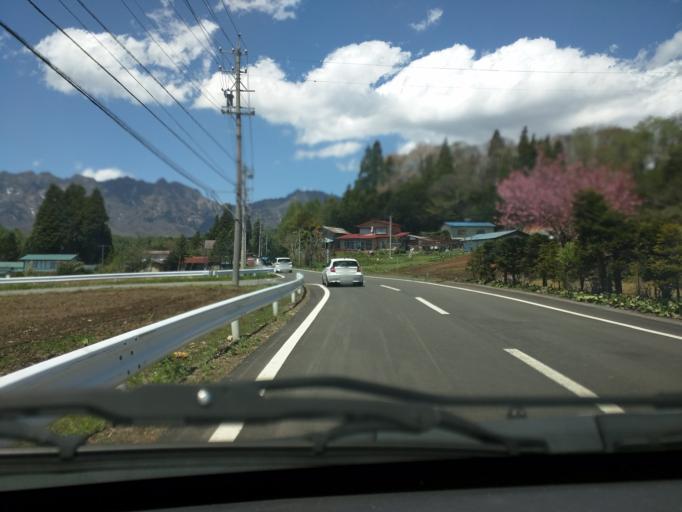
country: JP
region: Nagano
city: Nagano-shi
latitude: 36.7126
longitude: 138.0873
